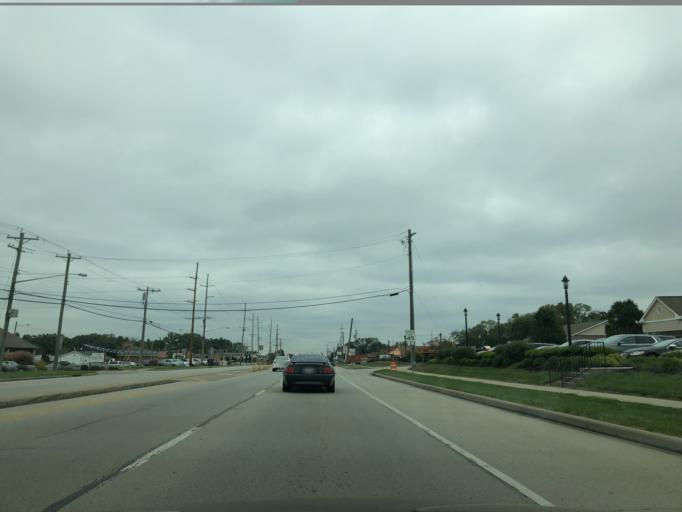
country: US
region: Ohio
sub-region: Warren County
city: Landen
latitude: 39.3037
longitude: -84.2826
